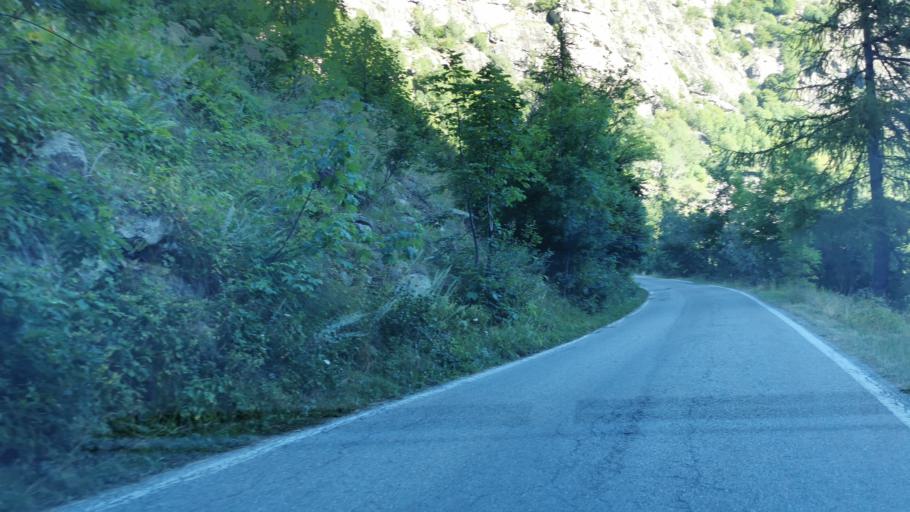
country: IT
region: Piedmont
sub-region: Provincia di Cuneo
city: Demonte
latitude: 44.2137
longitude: 7.2788
